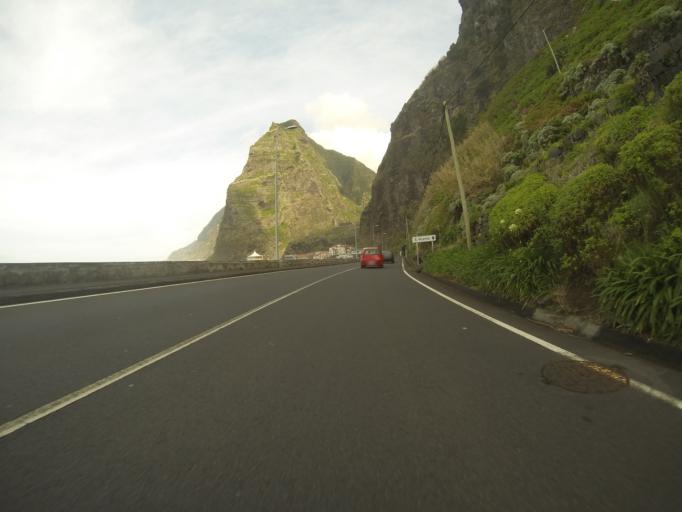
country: PT
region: Madeira
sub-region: Sao Vicente
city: Sao Vicente
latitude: 32.8088
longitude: -17.0540
